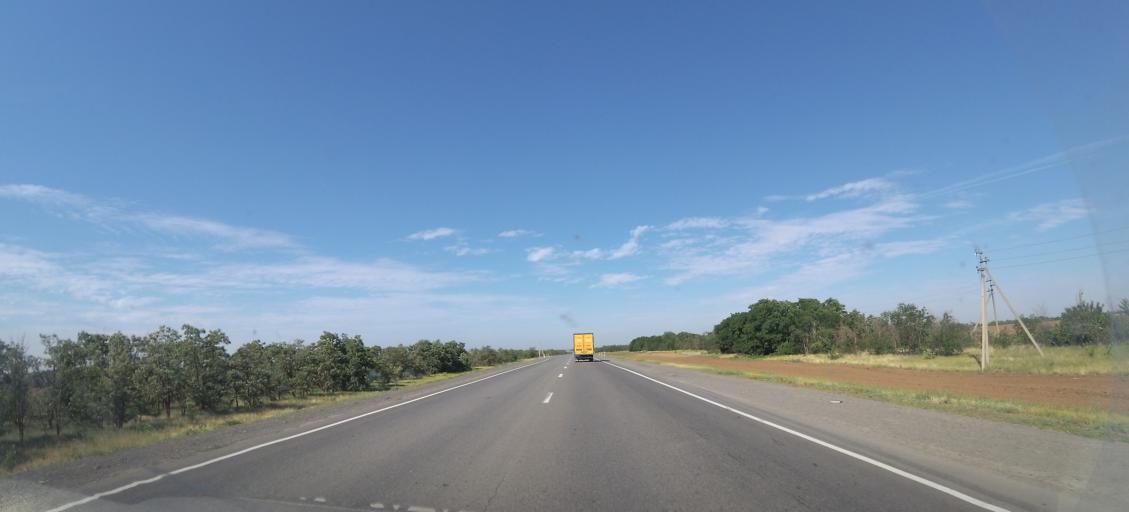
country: RU
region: Volgograd
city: Oktyabr'skiy
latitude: 48.6943
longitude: 43.7893
